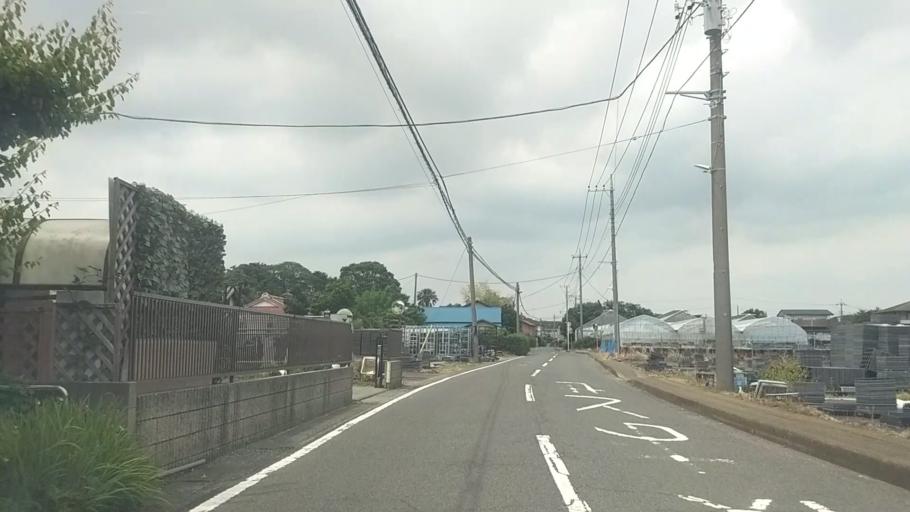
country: JP
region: Kanagawa
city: Chigasaki
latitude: 35.3898
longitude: 139.4142
